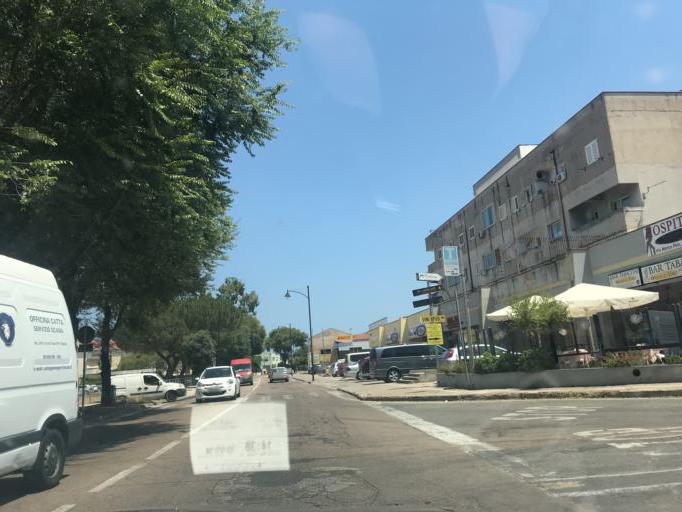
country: IT
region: Sardinia
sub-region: Provincia di Olbia-Tempio
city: Olbia
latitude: 40.9165
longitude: 9.4951
